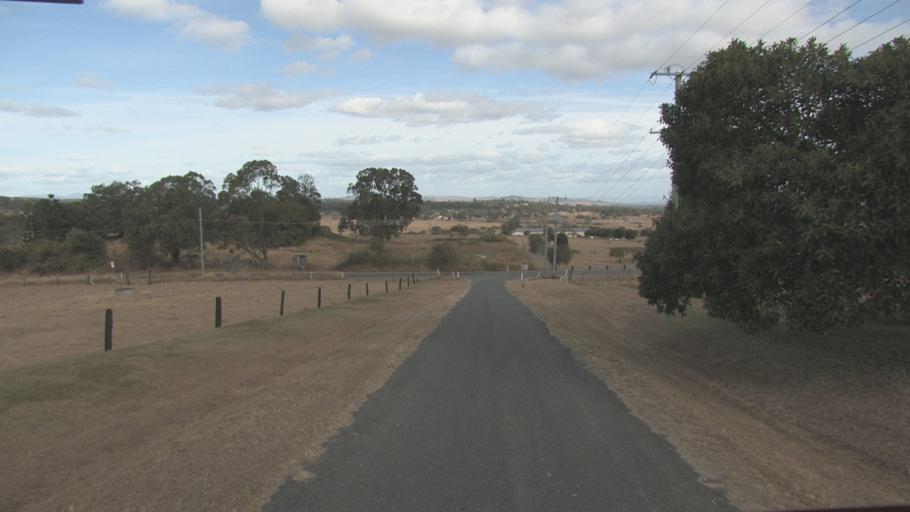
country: AU
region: Queensland
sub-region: Logan
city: Cedar Vale
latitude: -27.9147
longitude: 152.9960
